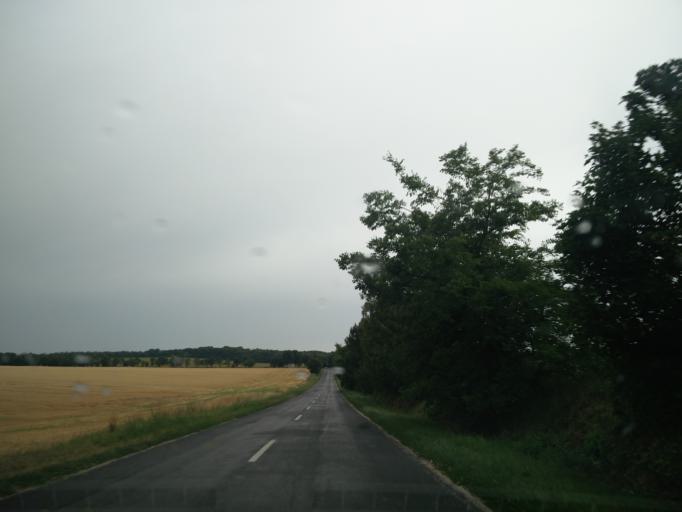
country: HU
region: Fejer
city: Bicske
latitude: 47.4342
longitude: 18.6455
